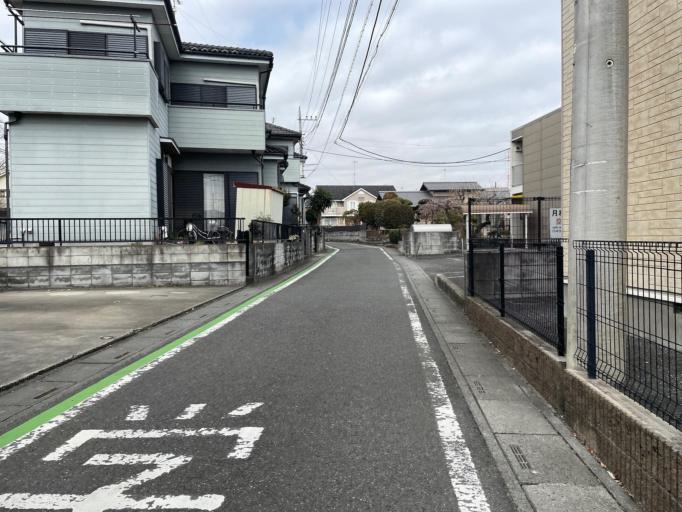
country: JP
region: Saitama
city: Ogawa
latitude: 36.0487
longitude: 139.3214
